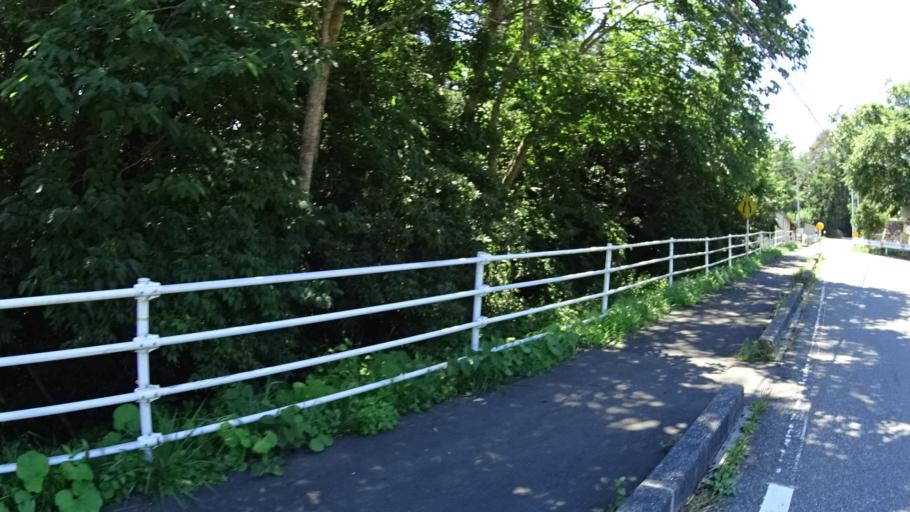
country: JP
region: Iwate
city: Ofunato
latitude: 38.8443
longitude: 141.6299
